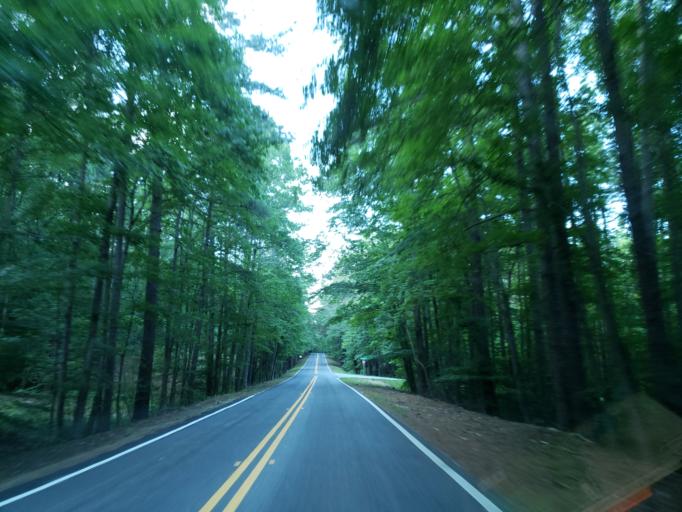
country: US
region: Georgia
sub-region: Bartow County
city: Emerson
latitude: 34.1772
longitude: -84.7371
